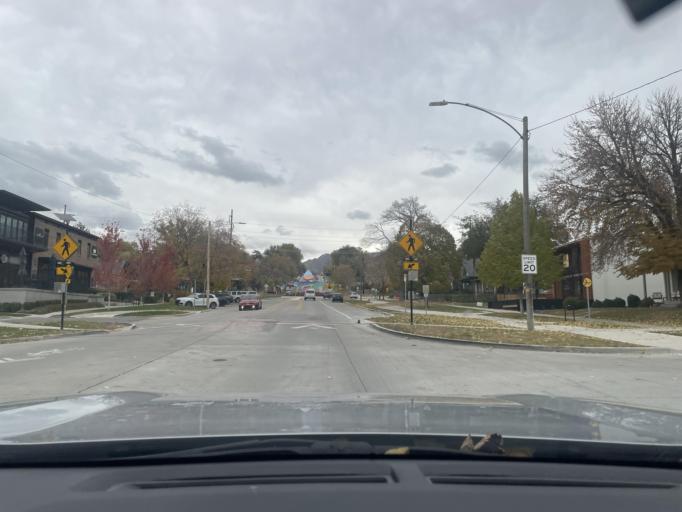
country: US
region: Utah
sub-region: Salt Lake County
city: Salt Lake City
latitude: 40.7498
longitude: -111.8612
